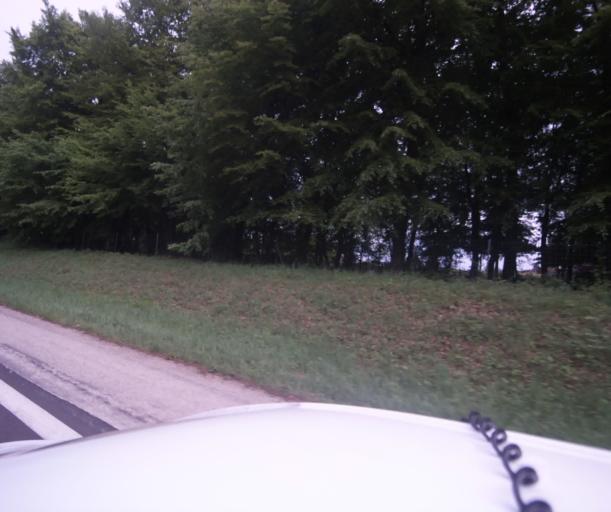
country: FR
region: Franche-Comte
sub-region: Departement du Doubs
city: Franois
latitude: 47.2131
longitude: 5.9287
